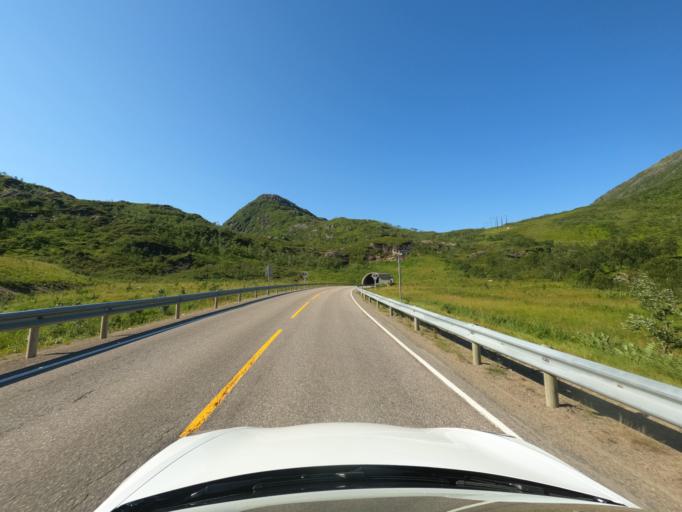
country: NO
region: Nordland
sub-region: Lodingen
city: Lodingen
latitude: 68.4882
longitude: 15.6890
